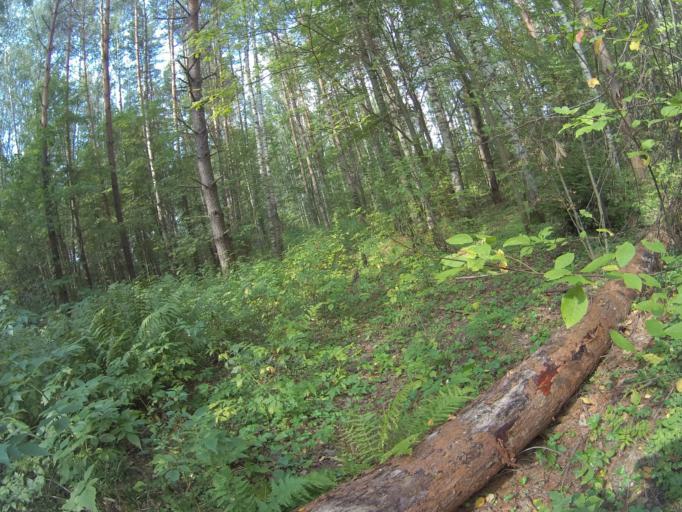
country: RU
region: Vladimir
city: Raduzhnyy
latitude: 55.9976
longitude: 40.2789
